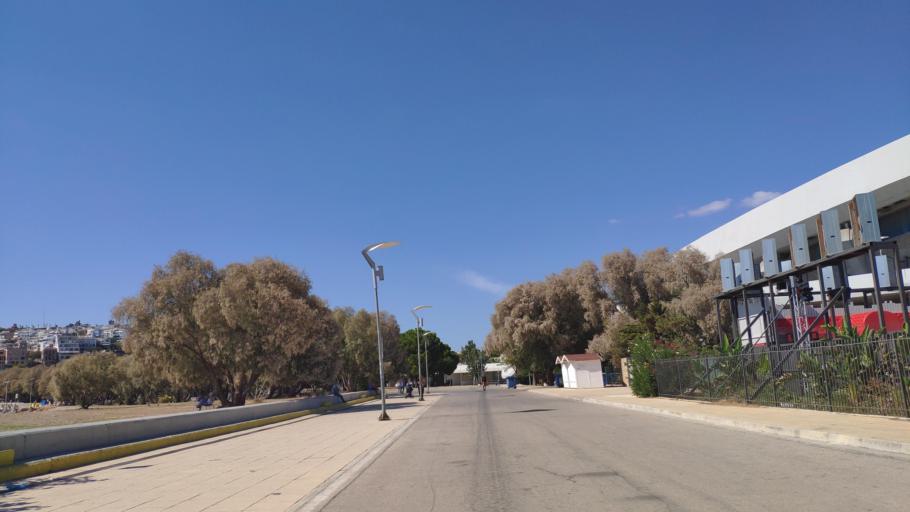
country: GR
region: Attica
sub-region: Nomarchia Athinas
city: Moskhaton
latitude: 37.9412
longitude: 23.6680
